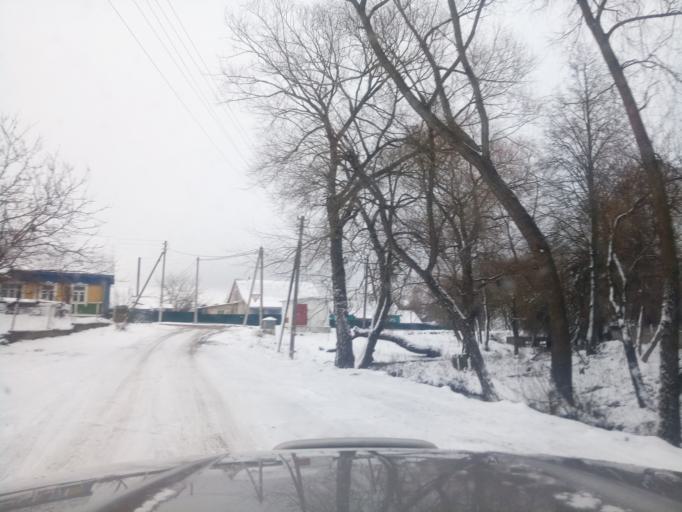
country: BY
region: Minsk
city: Kapyl'
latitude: 53.1558
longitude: 27.0809
